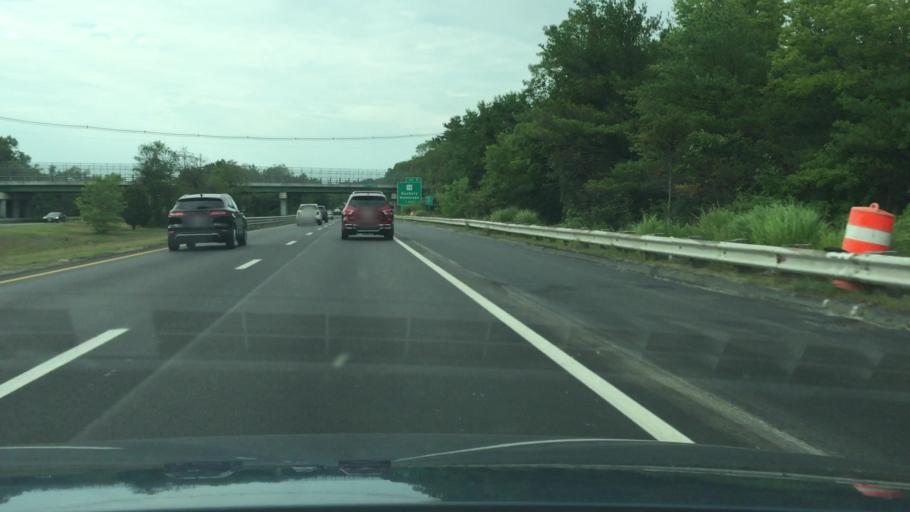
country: US
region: Massachusetts
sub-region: Plymouth County
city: Kingston
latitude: 42.0359
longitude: -70.7241
